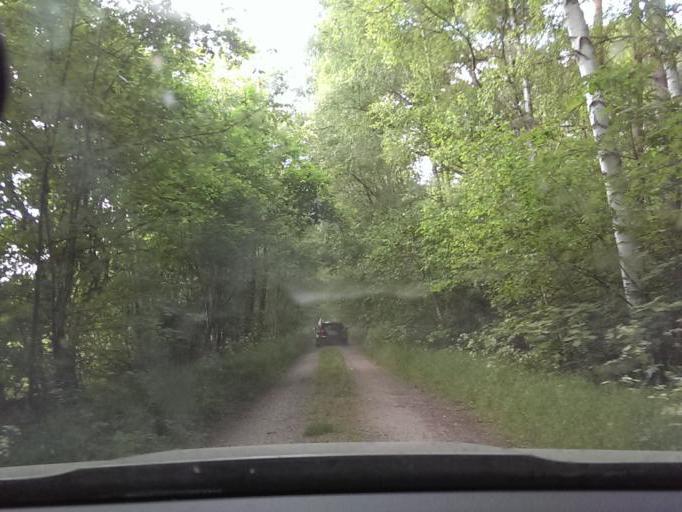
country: DE
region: Lower Saxony
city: Lindwedel
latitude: 52.5288
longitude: 9.6456
